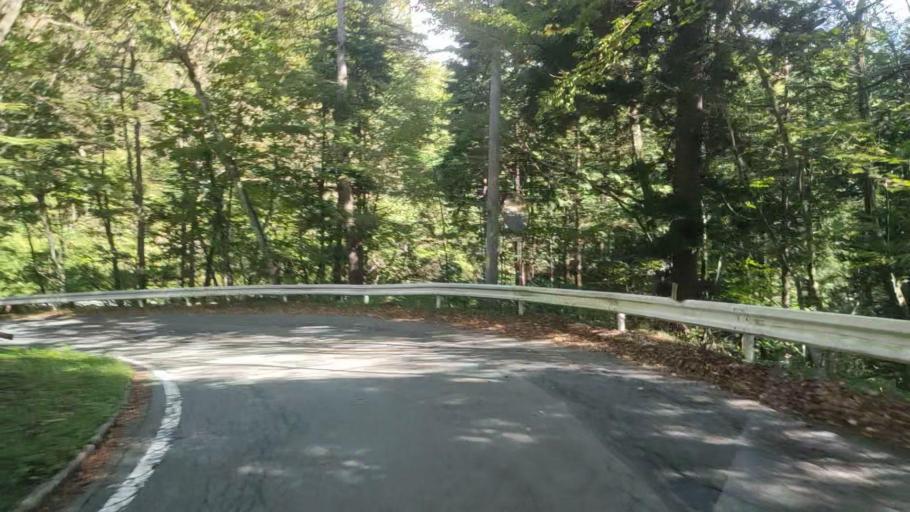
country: JP
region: Gunma
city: Nakanojomachi
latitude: 36.5972
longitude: 138.6873
